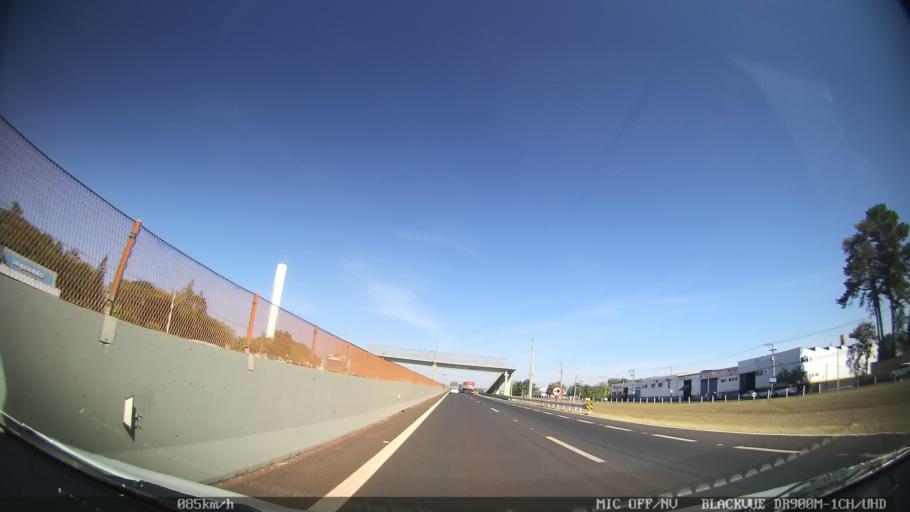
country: BR
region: Sao Paulo
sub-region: Ribeirao Preto
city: Ribeirao Preto
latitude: -21.1833
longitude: -47.7574
